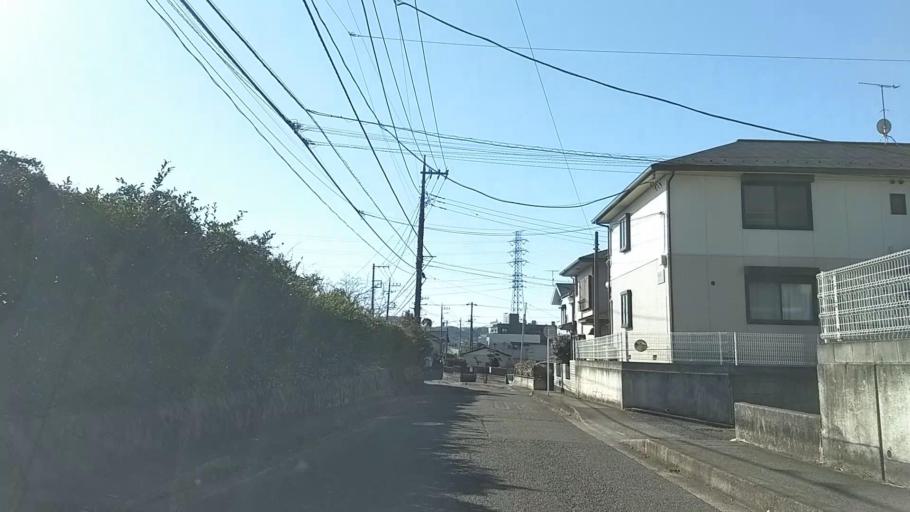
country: JP
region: Kanagawa
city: Hadano
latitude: 35.3857
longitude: 139.1977
